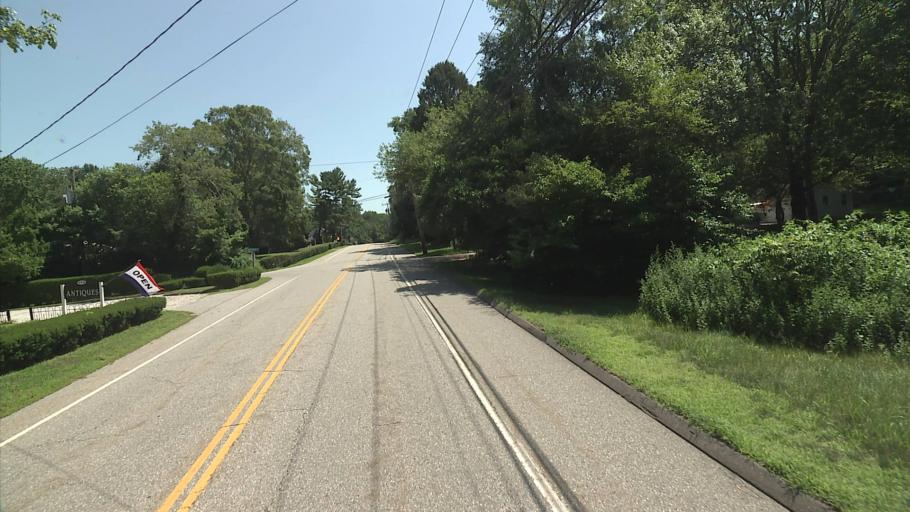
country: US
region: Connecticut
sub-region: Middlesex County
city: Essex Village
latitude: 41.3333
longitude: -72.3810
